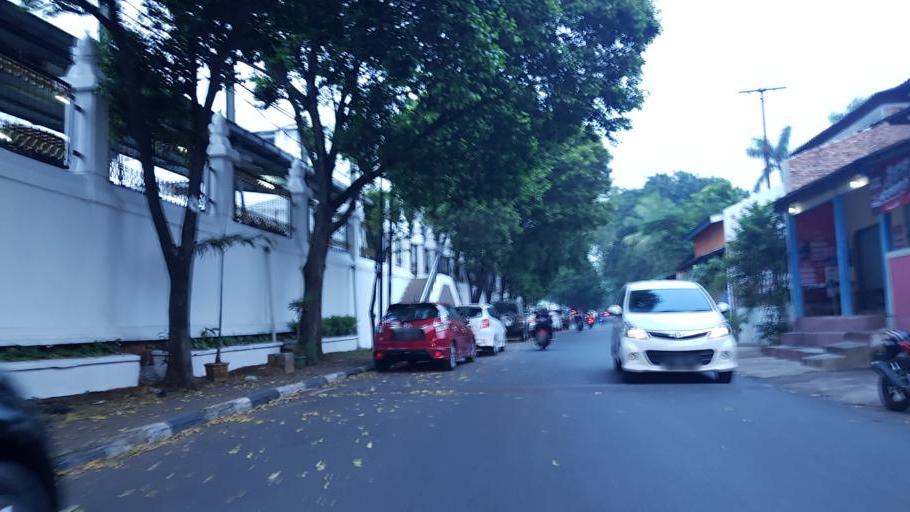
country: ID
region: West Java
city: Pamulang
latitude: -6.3136
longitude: 106.7889
